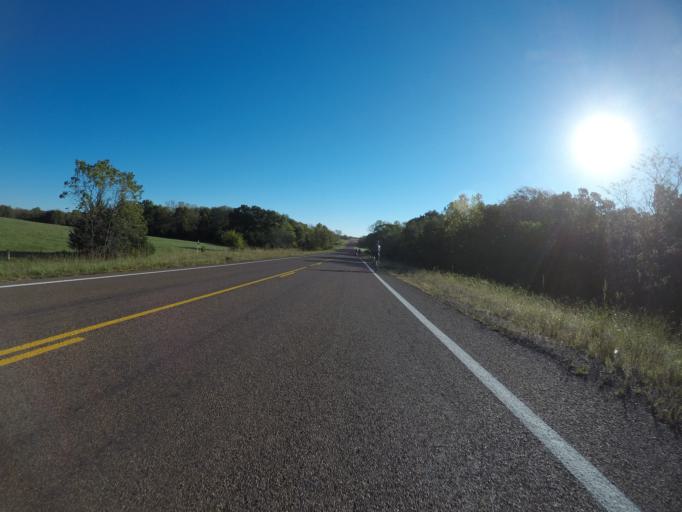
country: US
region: Kansas
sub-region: Douglas County
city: Eudora
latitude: 39.0011
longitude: -95.1427
